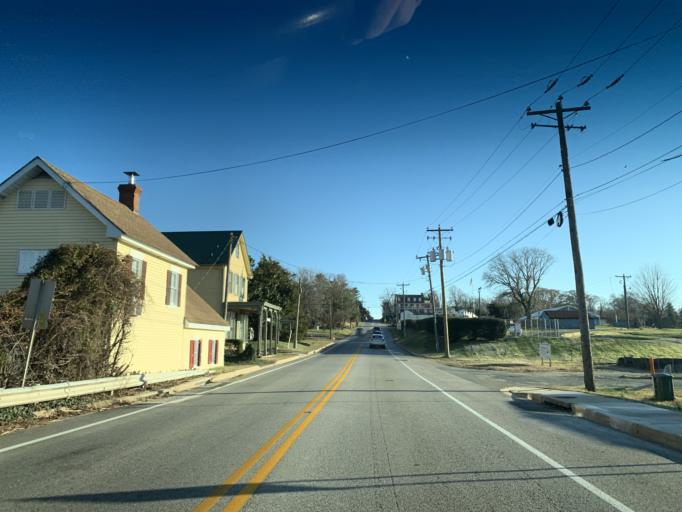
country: US
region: Delaware
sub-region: New Castle County
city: Middletown
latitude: 39.3634
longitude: -75.8815
